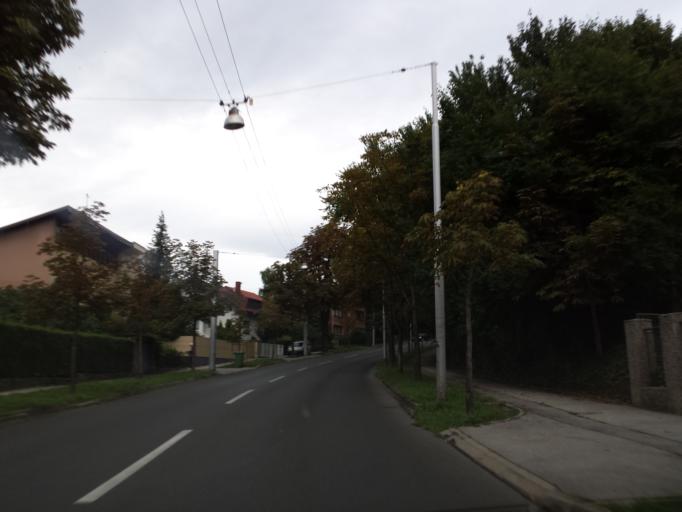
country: HR
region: Grad Zagreb
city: Zagreb
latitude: 45.8324
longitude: 15.9805
